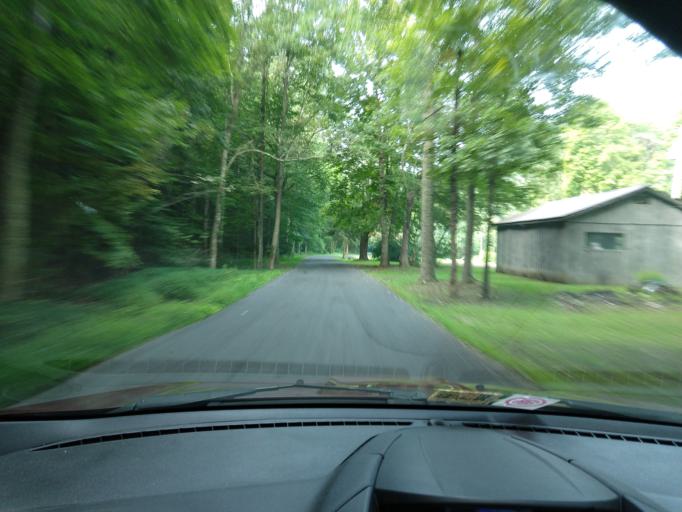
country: US
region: Virginia
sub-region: City of Covington
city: Covington
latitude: 37.8911
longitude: -80.0948
